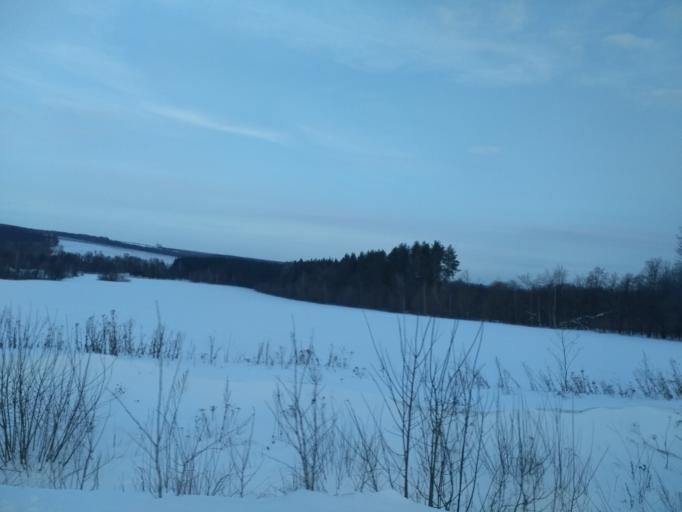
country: RU
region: Bashkortostan
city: Kudeyevskiy
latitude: 54.7154
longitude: 56.6330
